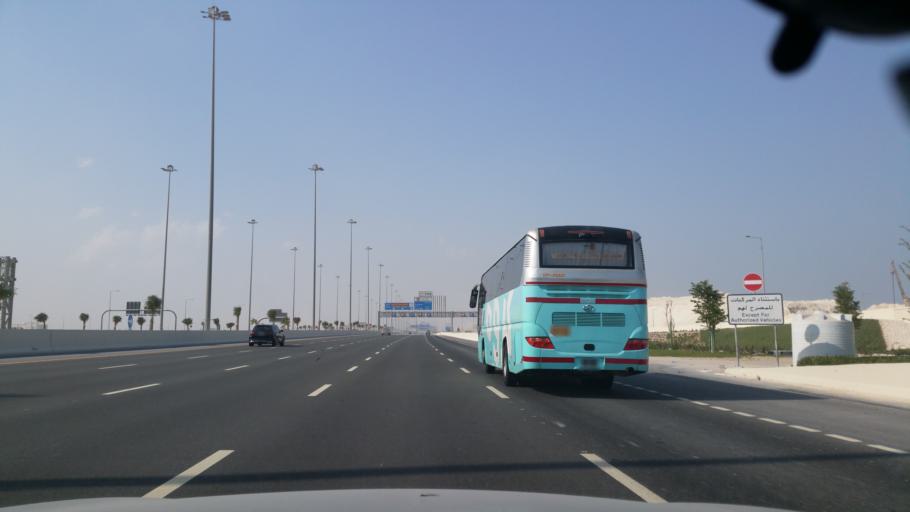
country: QA
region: Baladiyat Umm Salal
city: Umm Salal Muhammad
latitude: 25.4325
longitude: 51.4840
